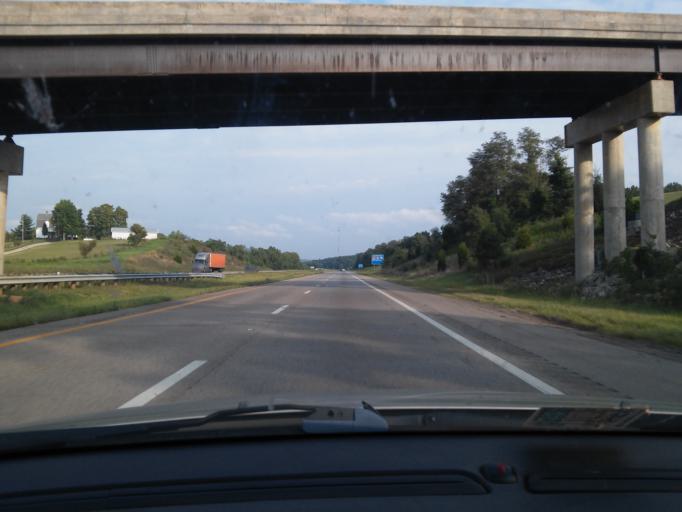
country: US
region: Ohio
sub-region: Gallia County
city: Gallipolis
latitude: 38.8597
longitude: -82.2535
